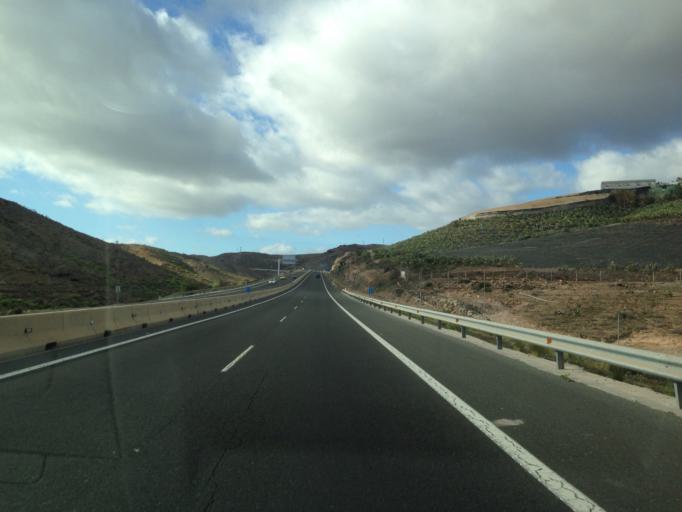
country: ES
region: Canary Islands
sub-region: Provincia de Las Palmas
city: Maspalomas
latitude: 27.7633
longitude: -15.6261
